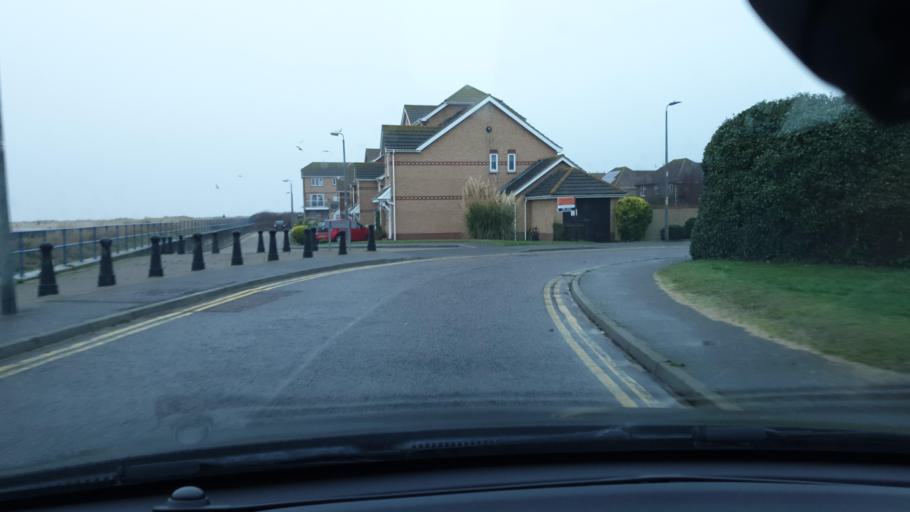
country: GB
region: England
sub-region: Essex
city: Clacton-on-Sea
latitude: 51.7791
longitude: 1.1369
